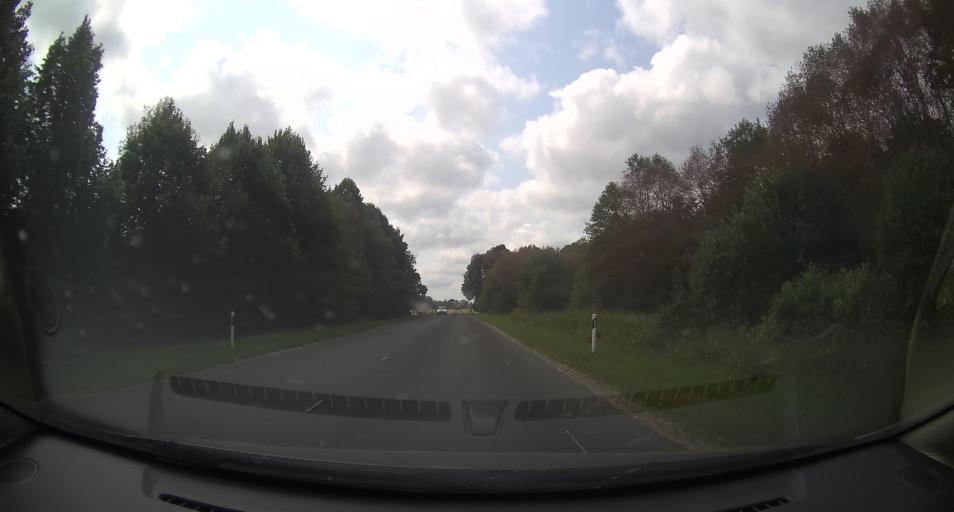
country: EE
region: Paernumaa
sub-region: Audru vald
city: Audru
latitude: 58.4719
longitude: 24.3236
